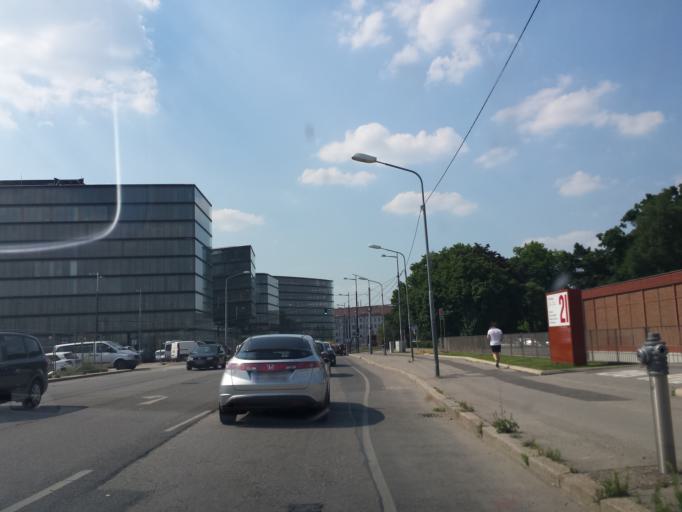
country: AT
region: Vienna
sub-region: Wien Stadt
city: Vienna
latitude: 48.1856
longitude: 16.3835
